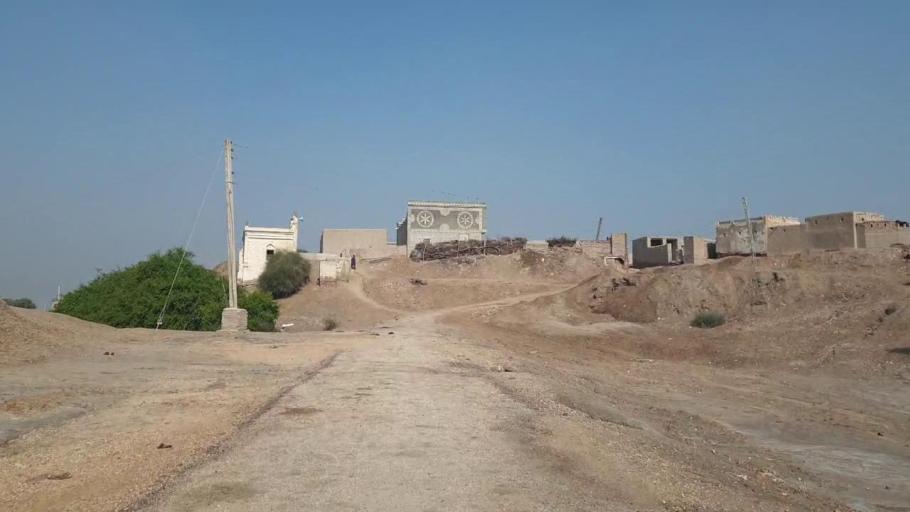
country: PK
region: Sindh
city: Sehwan
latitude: 26.4277
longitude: 67.7960
